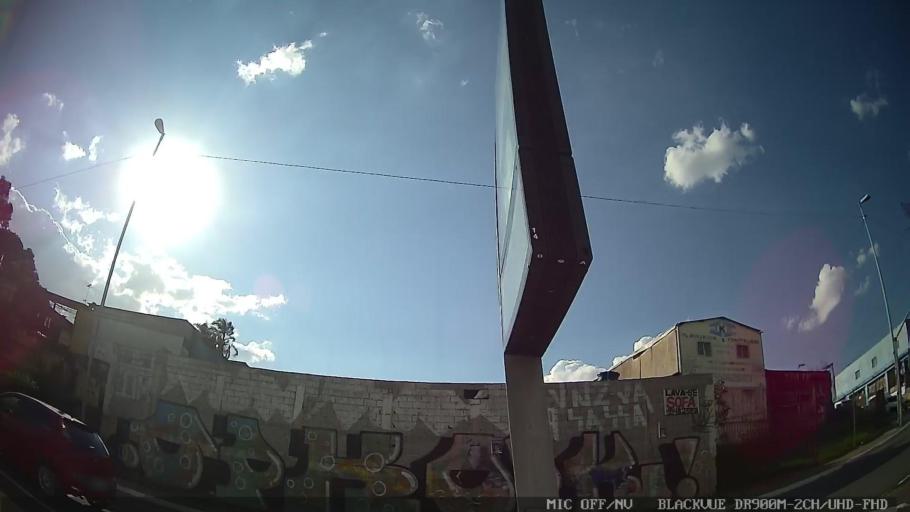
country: BR
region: Sao Paulo
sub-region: Ferraz De Vasconcelos
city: Ferraz de Vasconcelos
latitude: -23.5280
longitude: -46.4463
